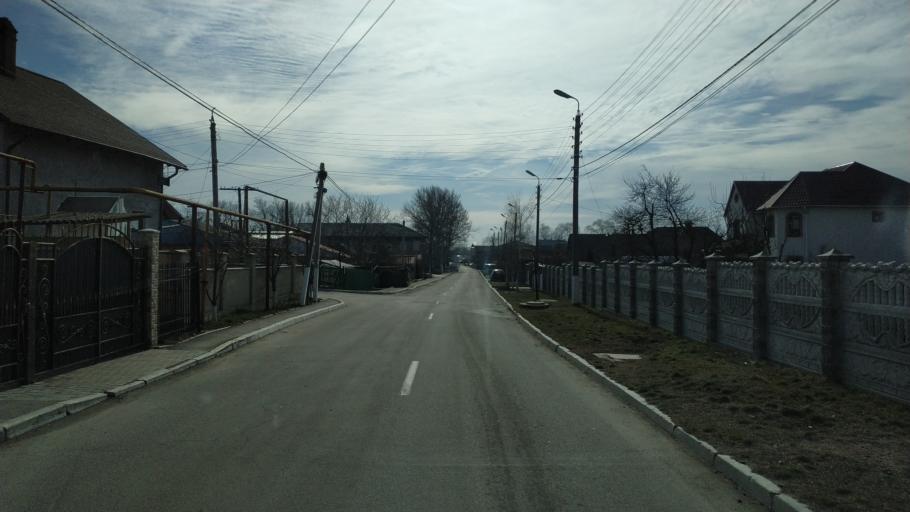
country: MD
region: Hincesti
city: Hincesti
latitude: 46.8312
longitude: 28.6038
